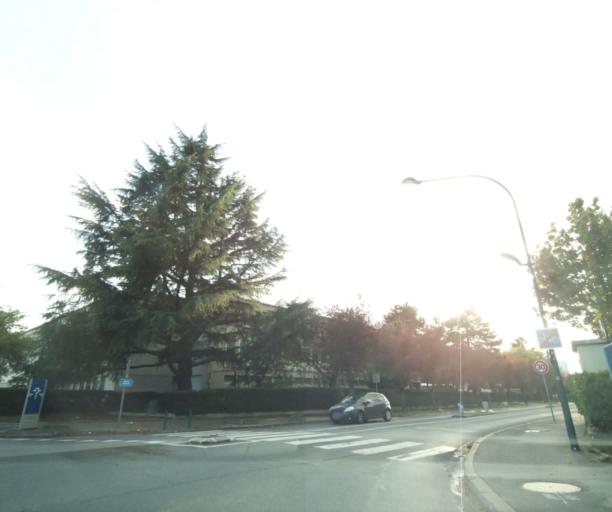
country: FR
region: Ile-de-France
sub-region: Departement des Hauts-de-Seine
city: Chatenay-Malabry
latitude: 48.7792
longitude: 2.2463
